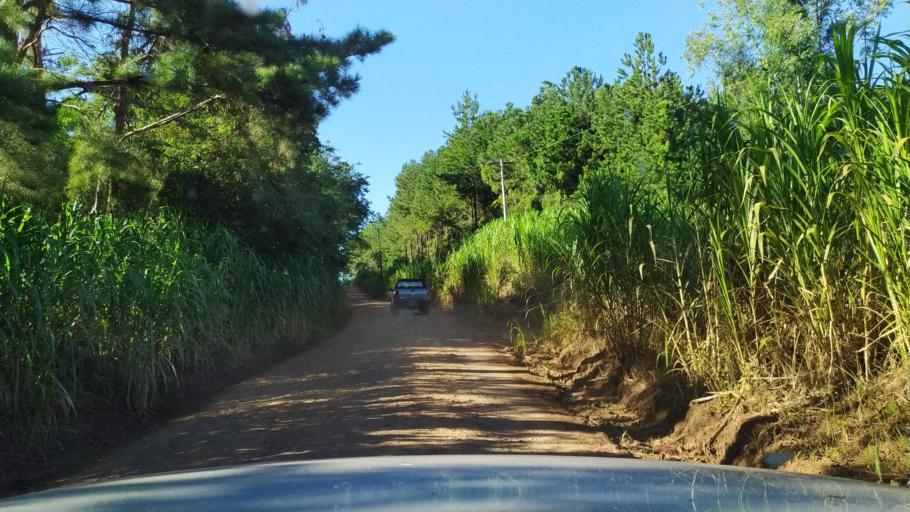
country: AR
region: Misiones
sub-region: Departamento de Montecarlo
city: Montecarlo
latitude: -26.6113
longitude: -54.6985
